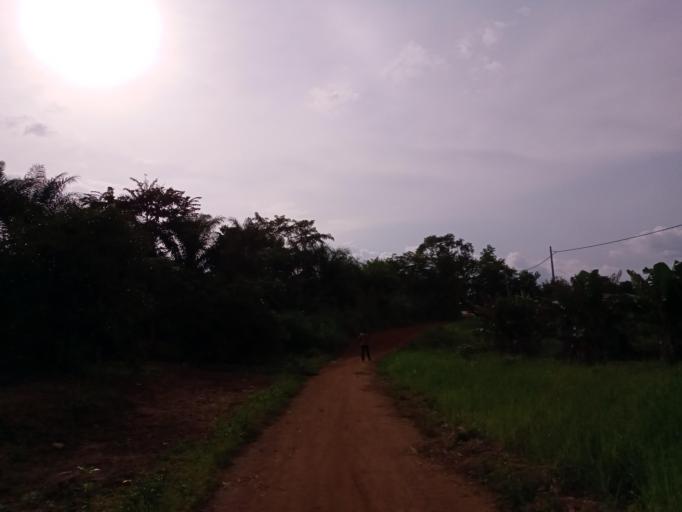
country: SL
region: Northern Province
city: Bumbuna
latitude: 9.0459
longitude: -11.7581
